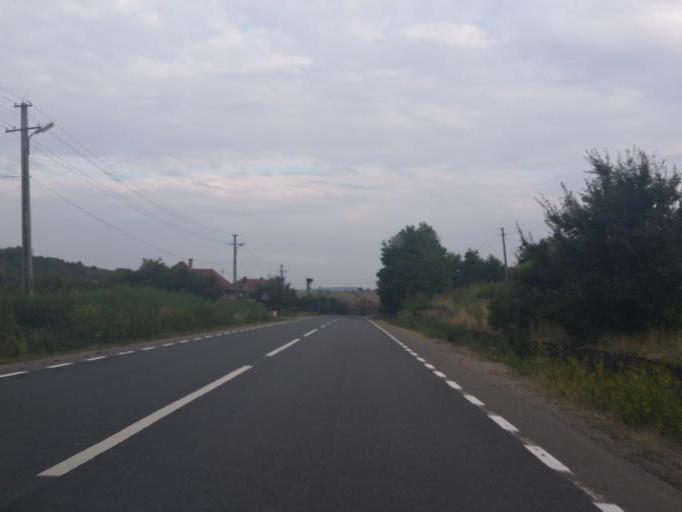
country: RO
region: Cluj
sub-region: Comuna Sanpaul
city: Sanpaul
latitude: 46.9330
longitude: 23.3943
